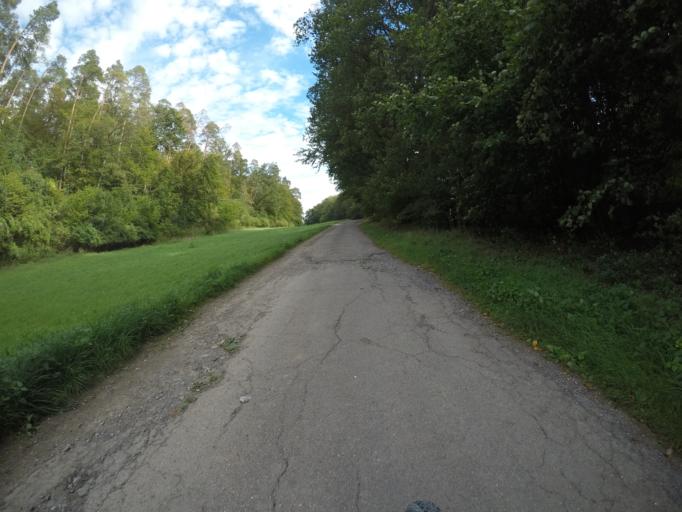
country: DE
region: Baden-Wuerttemberg
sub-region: Regierungsbezirk Stuttgart
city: Eberdingen
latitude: 48.8452
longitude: 8.9667
